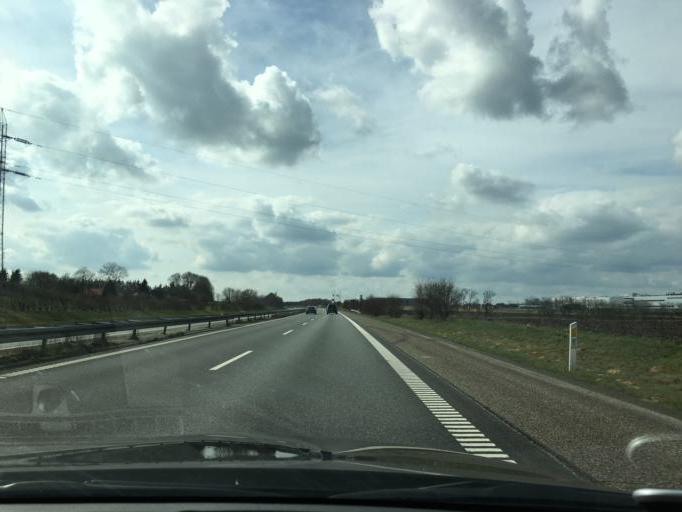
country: DK
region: South Denmark
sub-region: Vejen Kommune
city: Holsted
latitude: 55.5211
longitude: 8.9159
